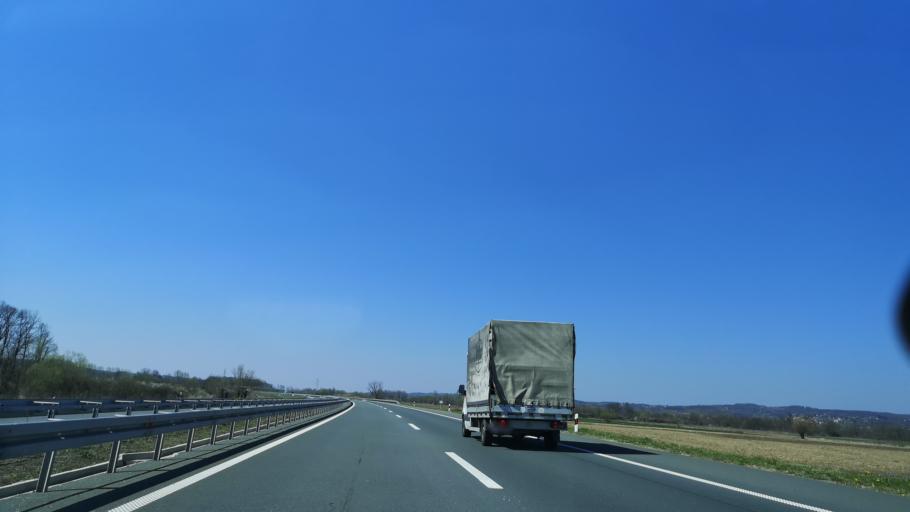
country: RS
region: Central Serbia
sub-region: Kolubarski Okrug
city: Ljig
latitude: 44.2764
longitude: 20.2645
